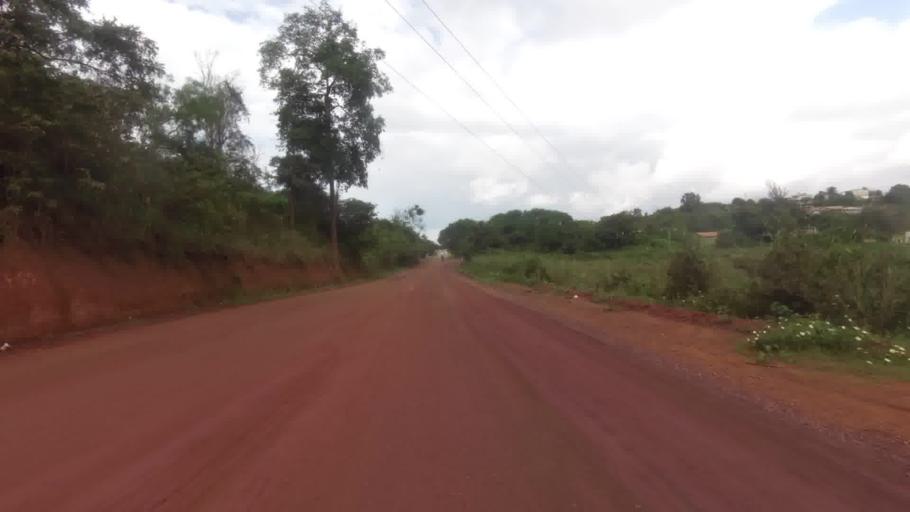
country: BR
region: Espirito Santo
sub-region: Piuma
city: Piuma
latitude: -20.7945
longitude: -40.6373
